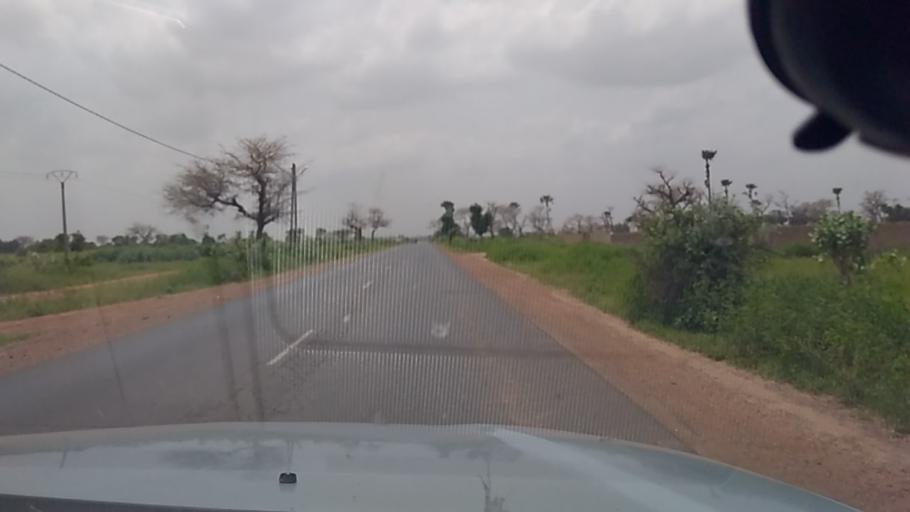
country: SN
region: Thies
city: Mekhe
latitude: 15.0024
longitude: -16.7458
